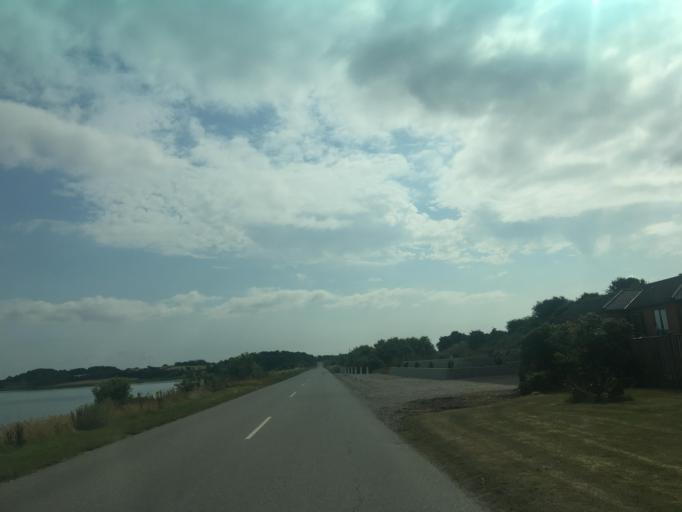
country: DK
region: North Denmark
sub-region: Thisted Kommune
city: Thisted
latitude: 56.8747
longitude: 8.6269
